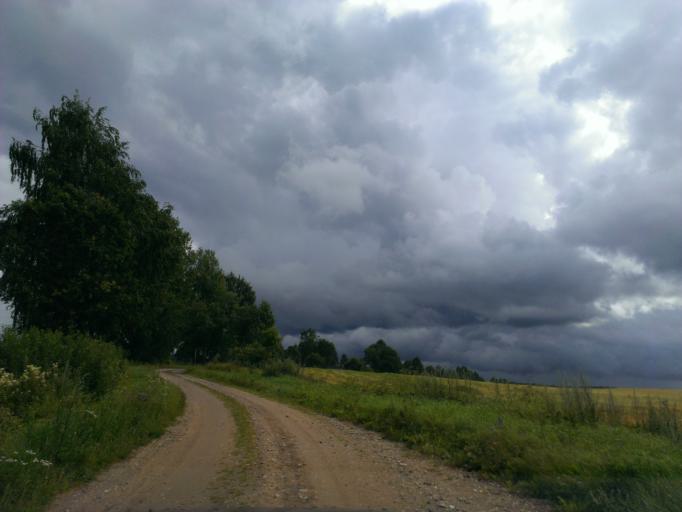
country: LV
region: Ligatne
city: Ligatne
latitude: 57.2072
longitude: 24.9494
